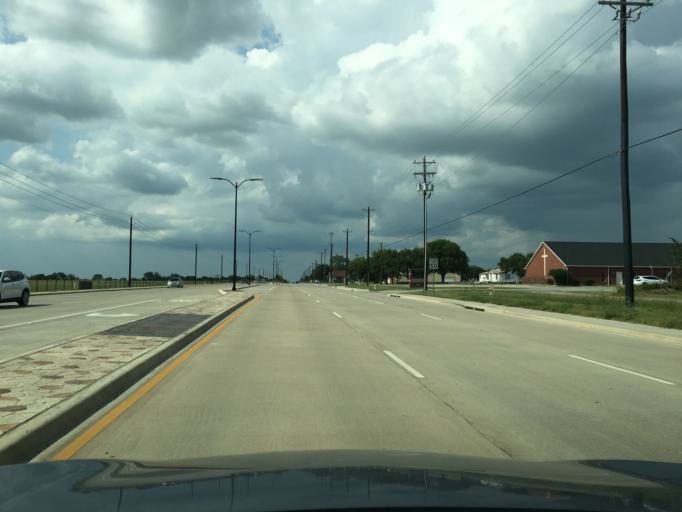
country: US
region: Texas
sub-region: Denton County
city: Oak Point
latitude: 33.1697
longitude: -96.9770
